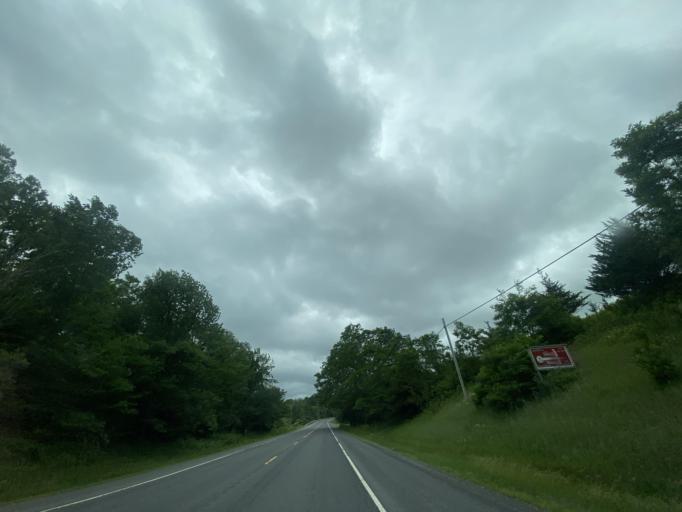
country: US
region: New York
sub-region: Greene County
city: Cairo
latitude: 42.3940
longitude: -73.9693
